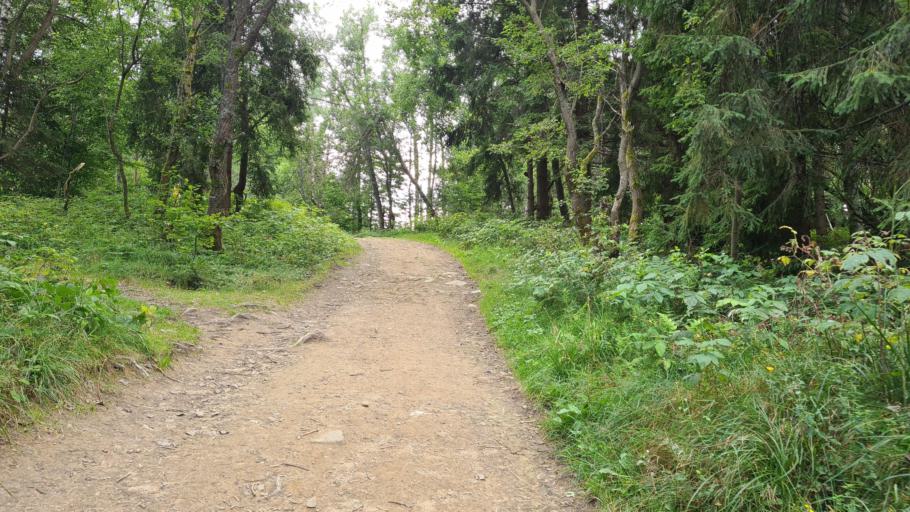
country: PL
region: Lesser Poland Voivodeship
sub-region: Powiat nowosadecki
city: Piwniczna-Zdroj
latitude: 49.4014
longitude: 20.6432
